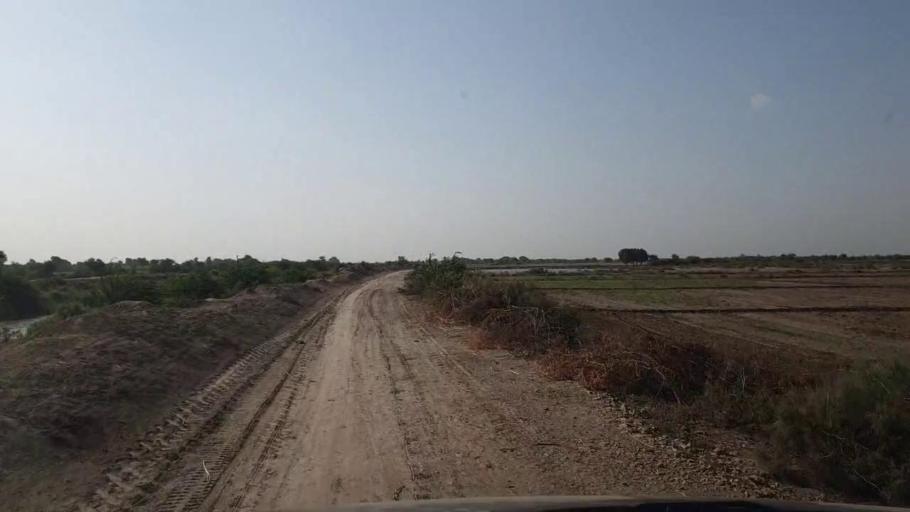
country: PK
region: Sindh
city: Kadhan
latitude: 24.6253
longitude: 69.0732
